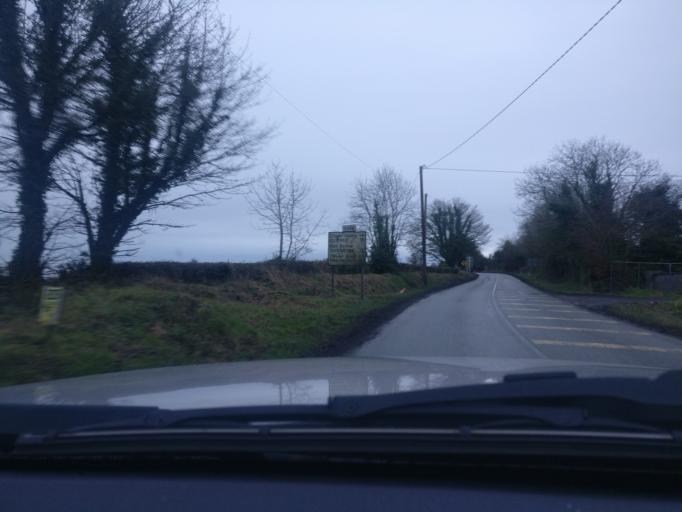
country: IE
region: Leinster
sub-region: Kildare
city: Kilcock
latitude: 53.4584
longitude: -6.6349
